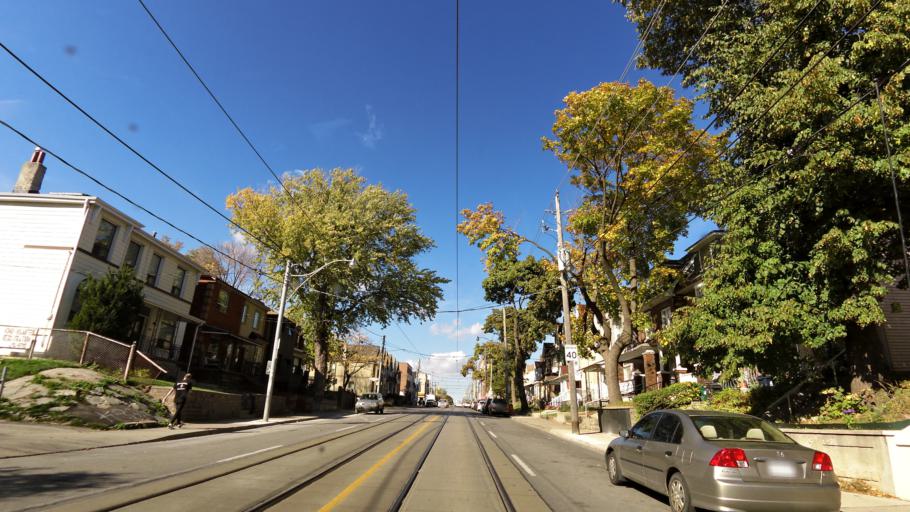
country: CA
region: Ontario
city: Toronto
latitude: 43.6530
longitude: -79.4222
